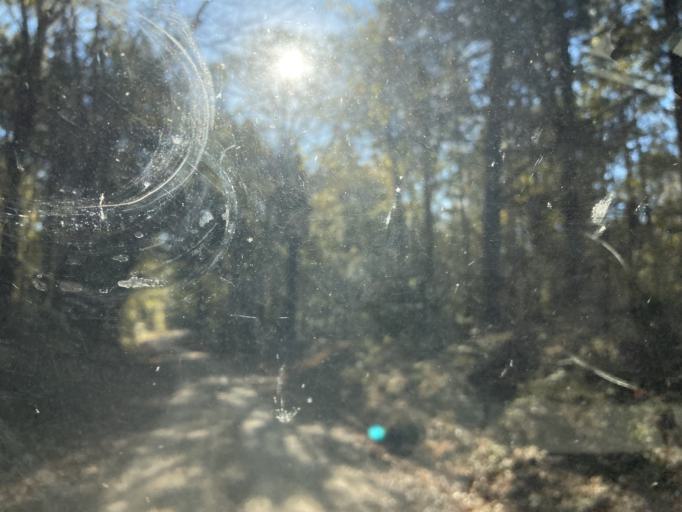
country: US
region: Mississippi
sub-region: Yazoo County
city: Yazoo City
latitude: 32.7853
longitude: -90.2821
